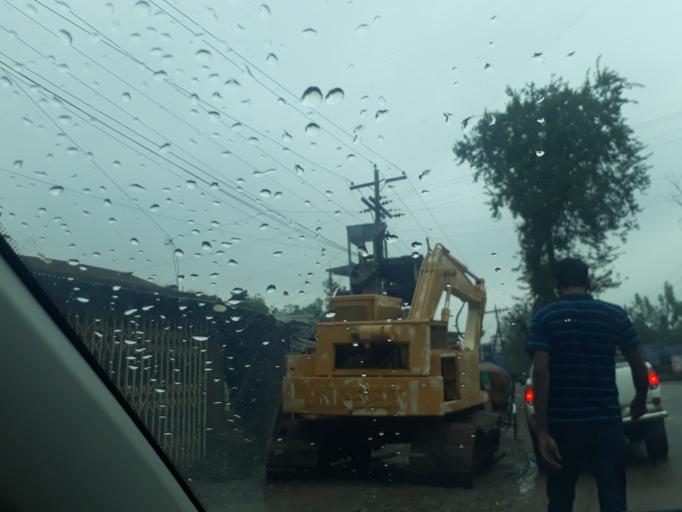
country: BD
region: Dhaka
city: Tungi
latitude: 23.9011
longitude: 90.3270
